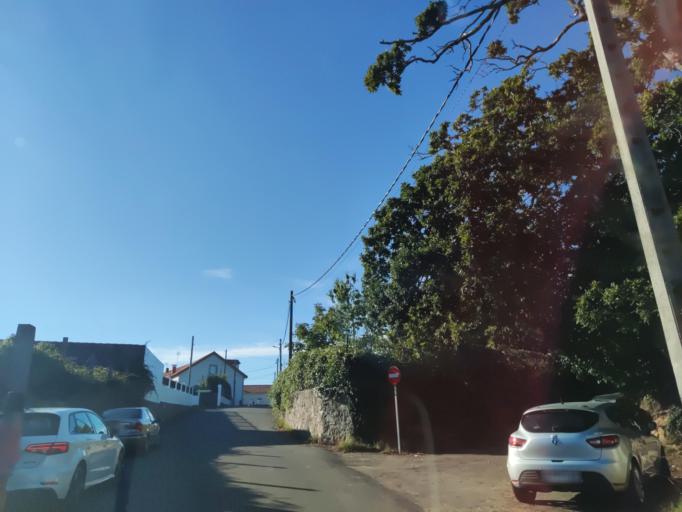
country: ES
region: Galicia
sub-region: Provincia da Coruna
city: Boiro
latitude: 42.5918
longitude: -8.9278
